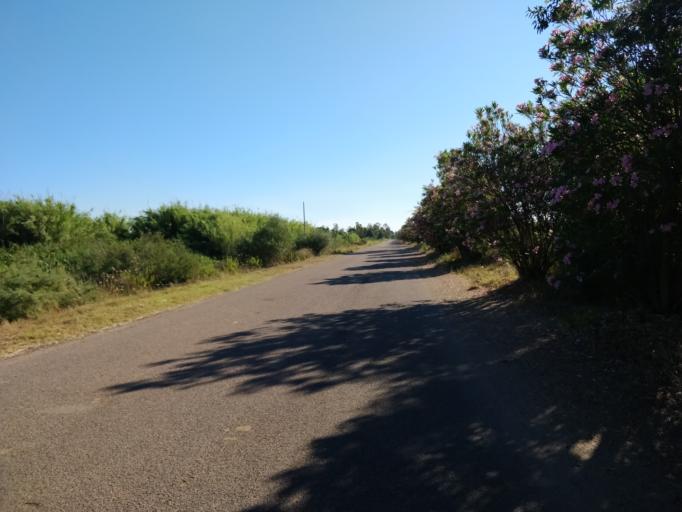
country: IT
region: Sardinia
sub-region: Provincia di Ogliastra
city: Girasole
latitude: 39.9546
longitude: 9.6719
